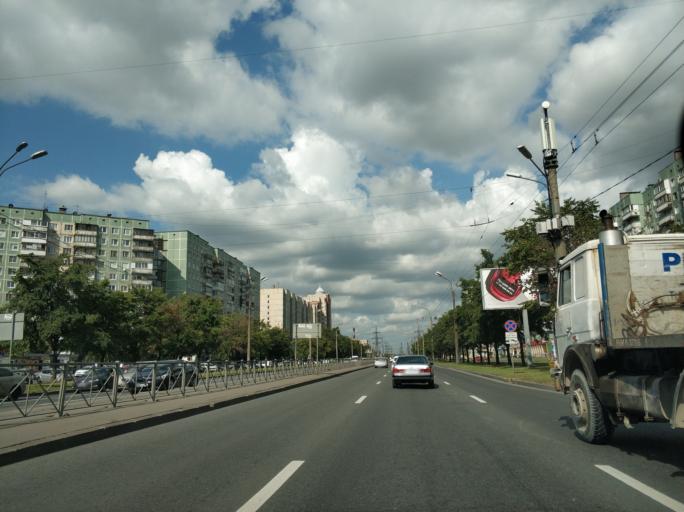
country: RU
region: St.-Petersburg
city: Krasnogvargeisky
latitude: 59.9519
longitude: 30.4712
